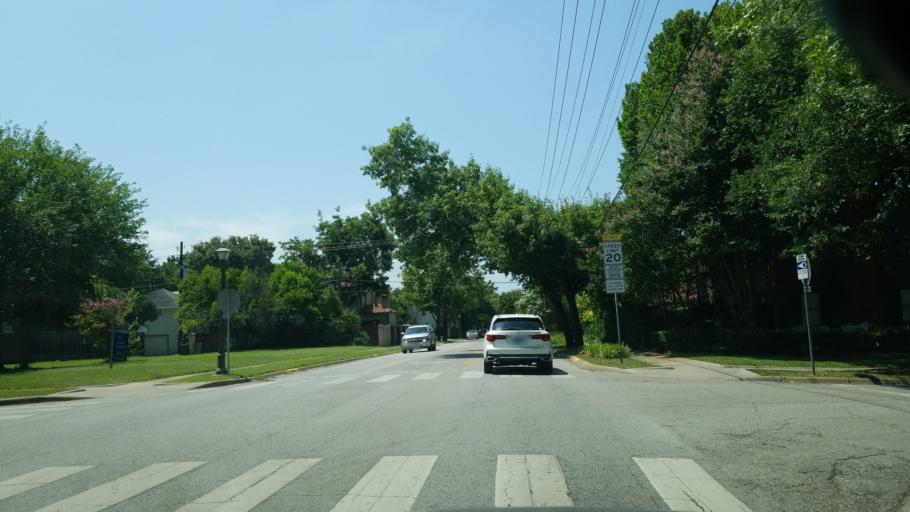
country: US
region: Texas
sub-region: Dallas County
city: Highland Park
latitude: 32.8346
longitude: -96.7872
